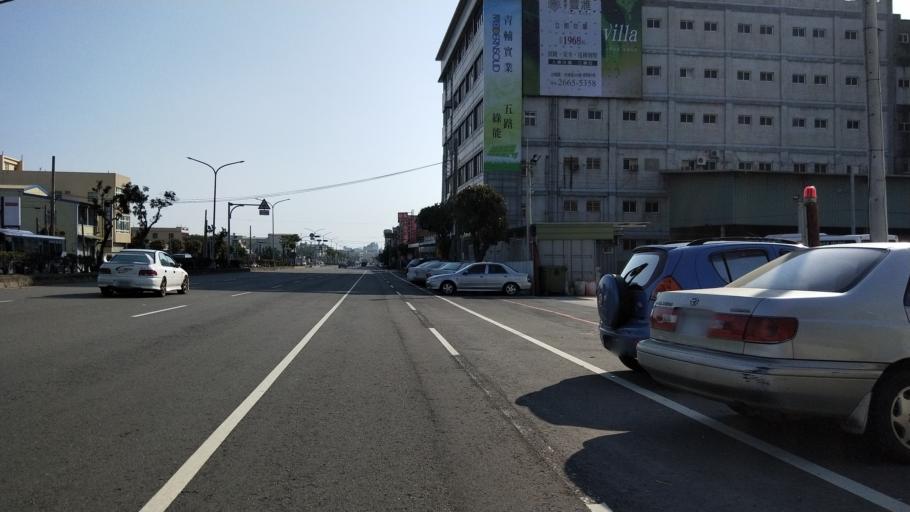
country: TW
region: Taiwan
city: Fengyuan
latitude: 24.2890
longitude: 120.5861
